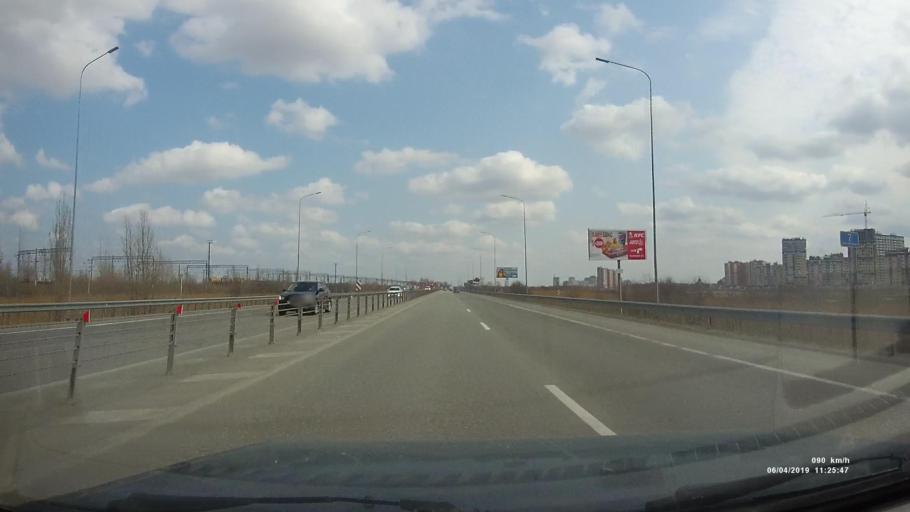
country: RU
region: Rostov
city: Bataysk
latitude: 47.1524
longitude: 39.7146
